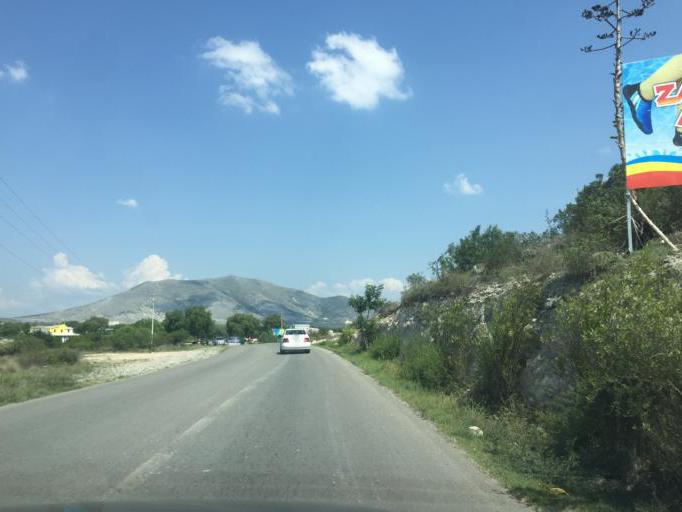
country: MX
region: Hidalgo
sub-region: Cardonal
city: Pozuelos
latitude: 20.6094
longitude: -99.1023
